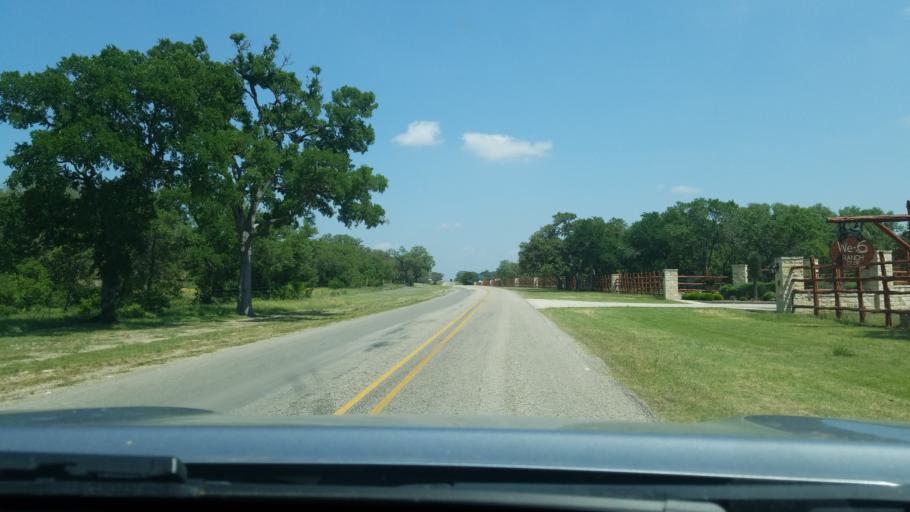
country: US
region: Texas
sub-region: Blanco County
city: Blanco
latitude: 29.9762
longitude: -98.5414
